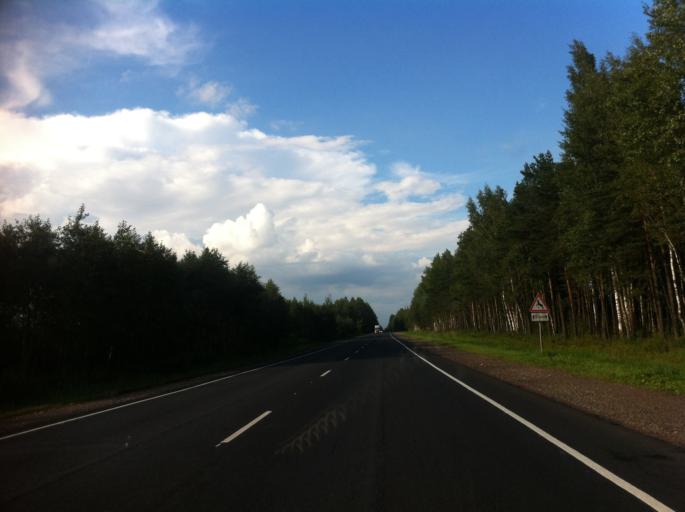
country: RU
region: Leningrad
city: Luga
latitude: 58.4533
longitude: 29.7594
